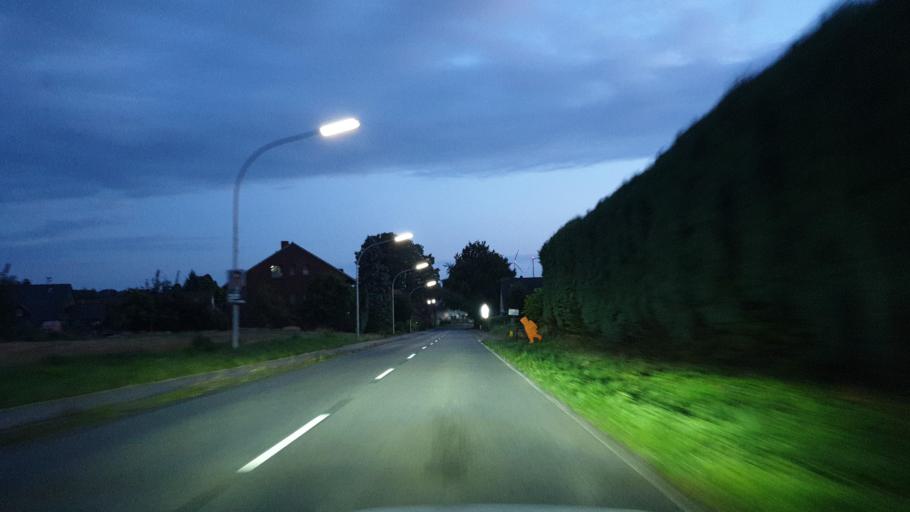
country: DE
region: North Rhine-Westphalia
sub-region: Regierungsbezirk Detmold
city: Huellhorst
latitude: 52.2576
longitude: 8.7016
